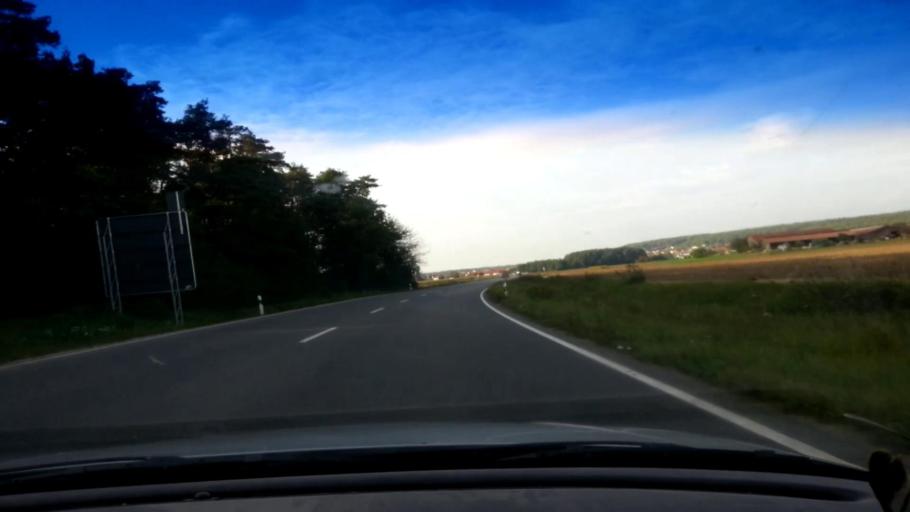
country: DE
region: Bavaria
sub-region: Upper Franconia
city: Strullendorf
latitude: 49.8321
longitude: 10.9782
